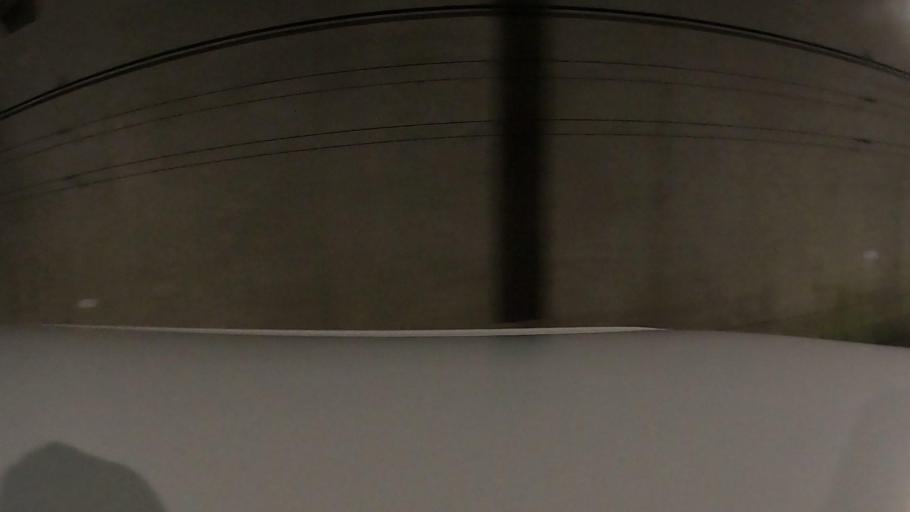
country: JP
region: Miyazaki
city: Nobeoka
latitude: 32.4756
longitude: 131.6280
